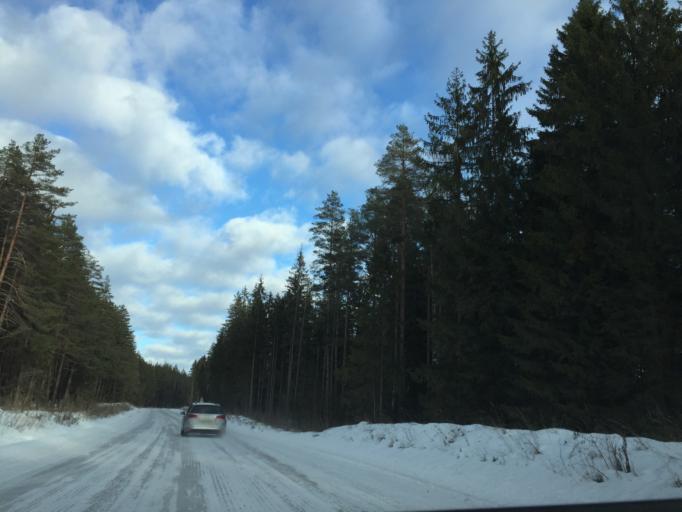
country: LV
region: Ogre
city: Jumprava
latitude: 56.5717
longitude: 24.9360
